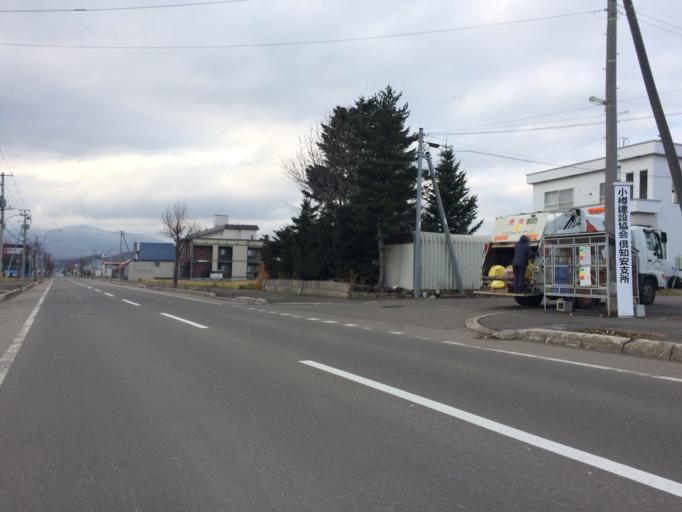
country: JP
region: Hokkaido
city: Niseko Town
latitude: 42.8983
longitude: 140.7658
